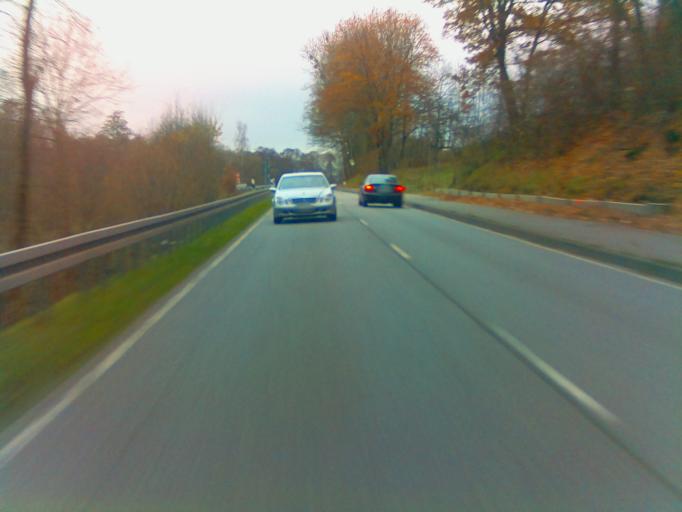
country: DE
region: Hesse
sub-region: Regierungsbezirk Darmstadt
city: Wald-Michelbach
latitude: 49.5826
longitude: 8.8476
